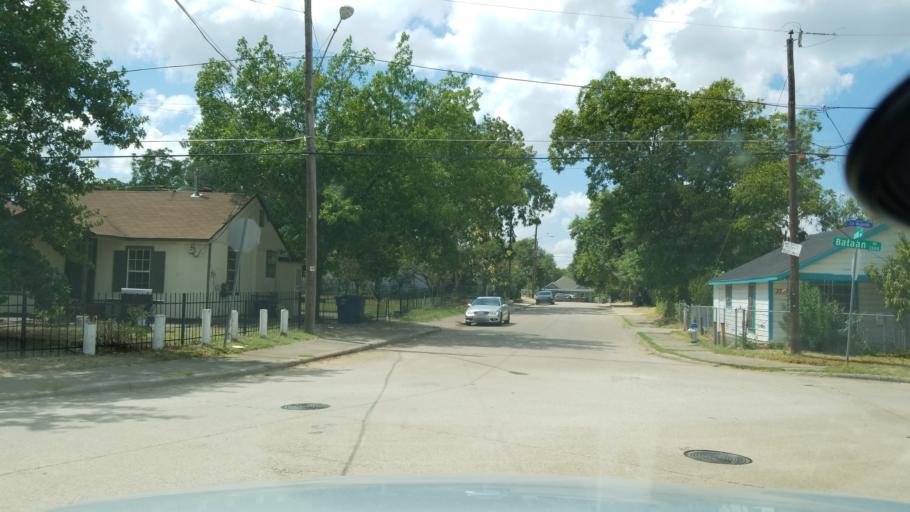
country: US
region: Texas
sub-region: Dallas County
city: Dallas
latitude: 32.7814
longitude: -96.8320
